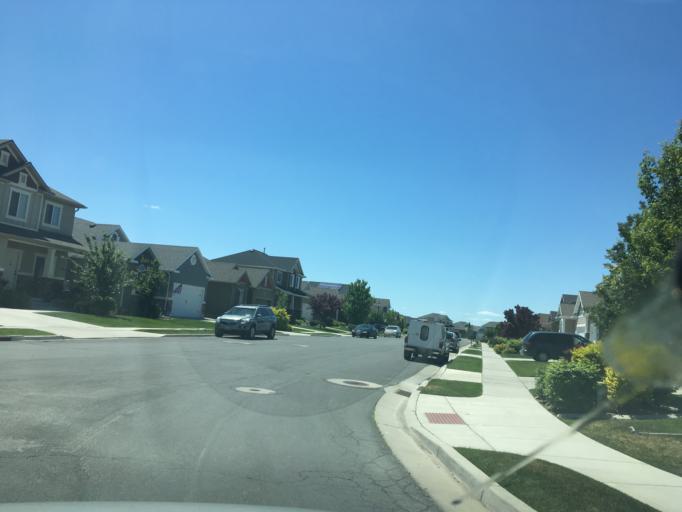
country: US
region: Utah
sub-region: Davis County
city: Layton
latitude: 41.0535
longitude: -112.0090
